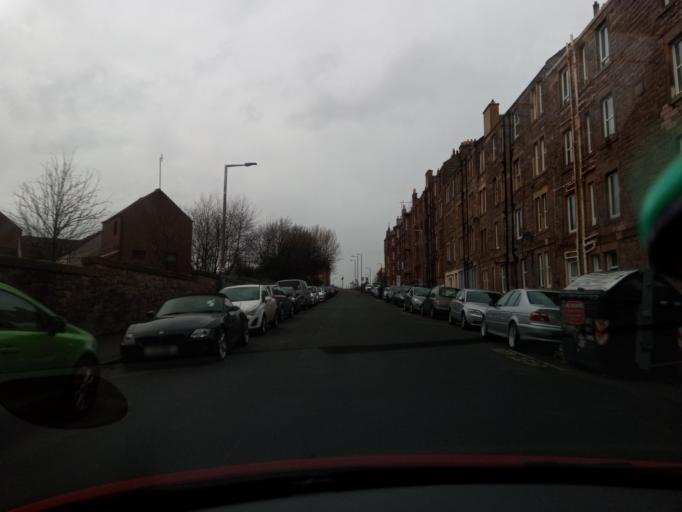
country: GB
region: Scotland
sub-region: West Lothian
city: Seafield
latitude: 55.9579
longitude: -3.1202
